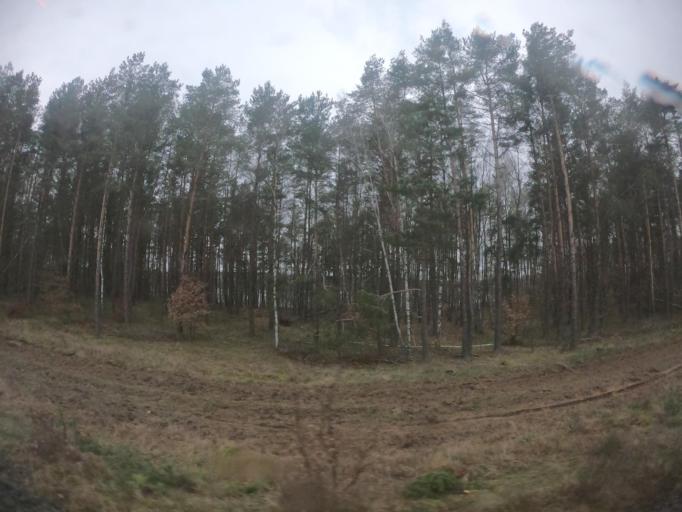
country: PL
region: West Pomeranian Voivodeship
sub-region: Powiat szczecinecki
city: Bialy Bor
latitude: 53.8499
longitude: 16.8722
